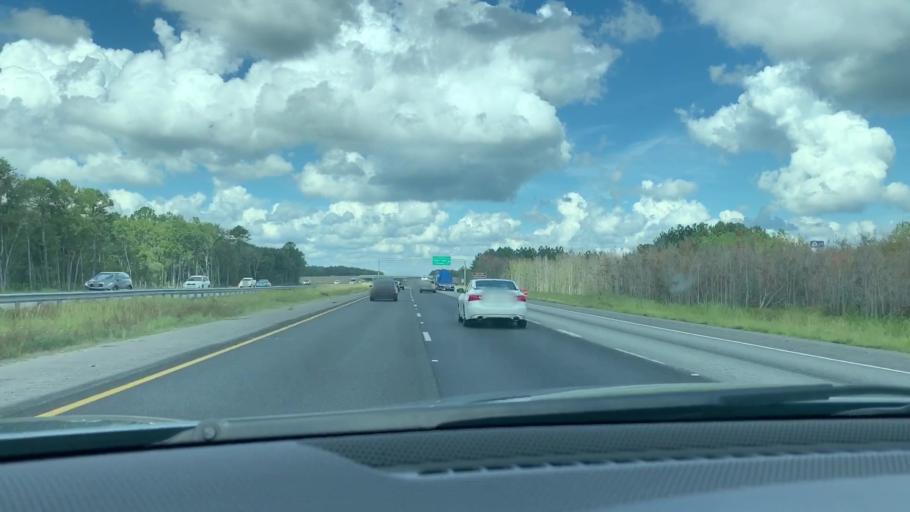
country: US
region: Georgia
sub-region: Camden County
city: Kingsland
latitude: 30.8181
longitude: -81.6648
